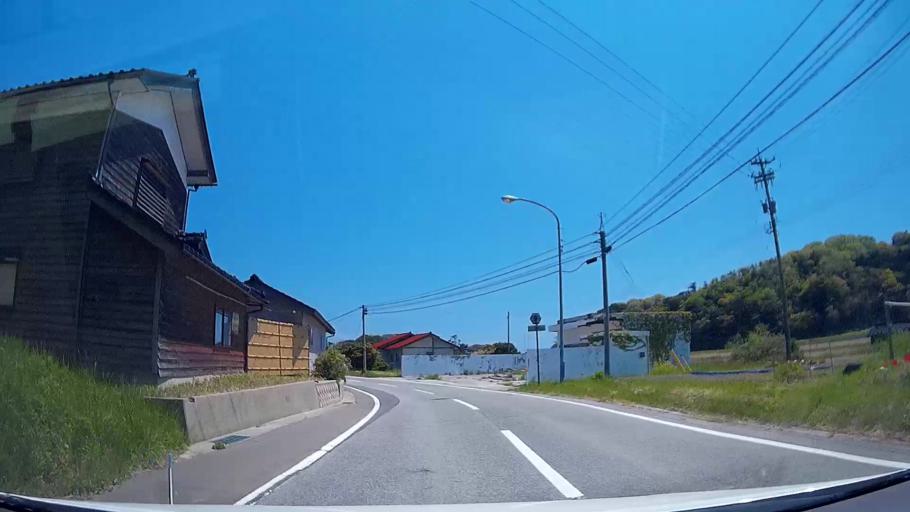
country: JP
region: Ishikawa
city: Nanao
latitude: 37.5256
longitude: 137.3211
